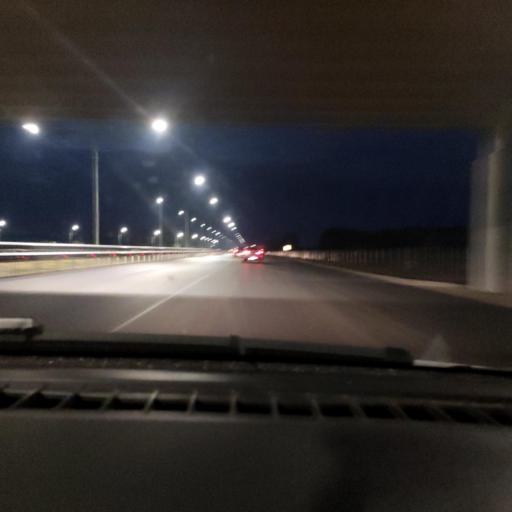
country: RU
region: Voronezj
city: Ramon'
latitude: 52.0083
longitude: 39.2122
